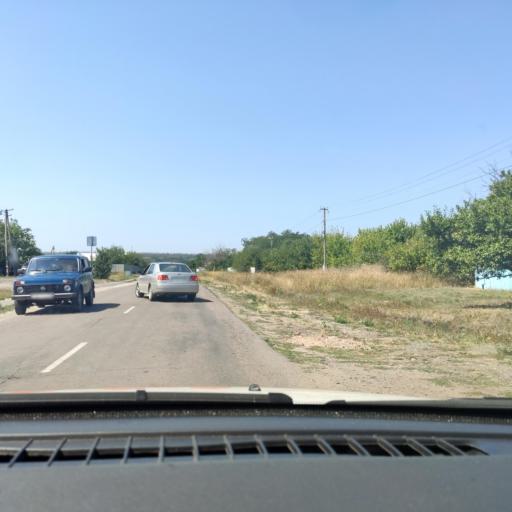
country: RU
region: Voronezj
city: Imeni Pervogo Maya
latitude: 50.7185
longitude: 39.3801
